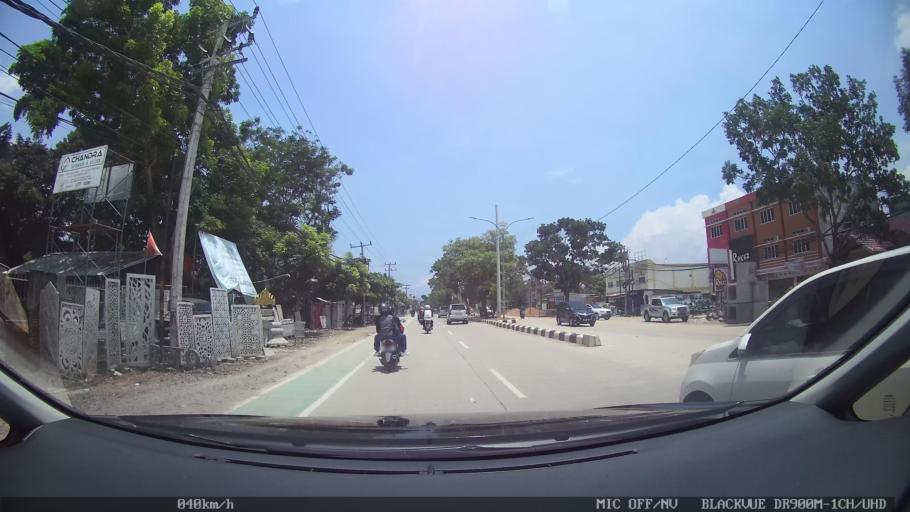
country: ID
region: Lampung
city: Kedaton
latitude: -5.3720
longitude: 105.2975
